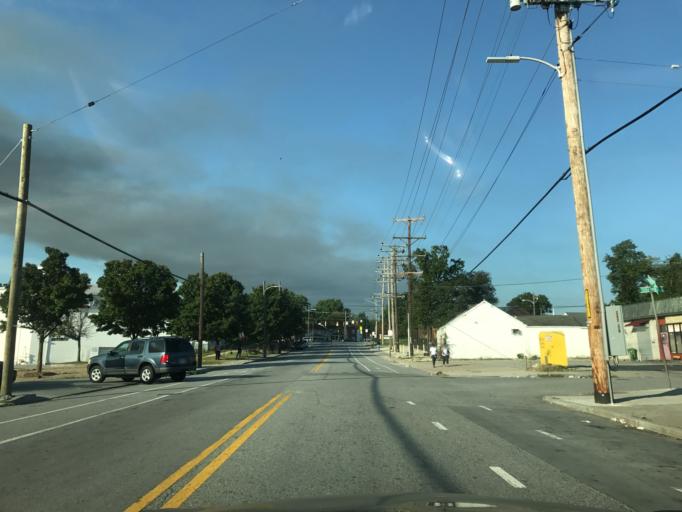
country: US
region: Maryland
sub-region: Baltimore County
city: Baltimore Highlands
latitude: 39.2499
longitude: -76.6233
